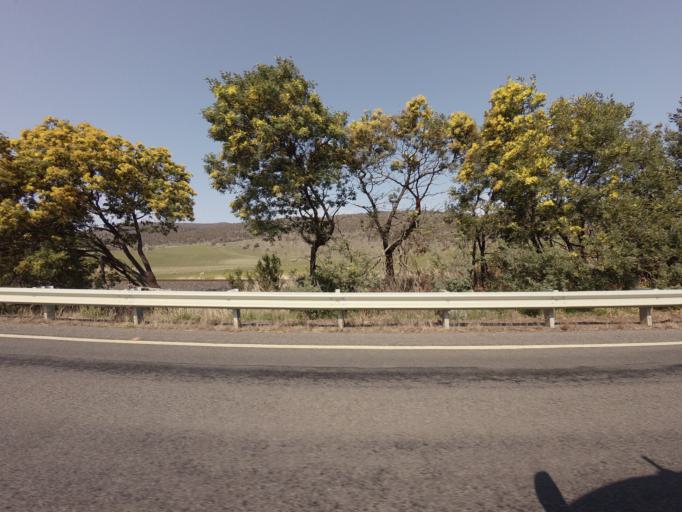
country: AU
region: Tasmania
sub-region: Northern Midlands
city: Evandale
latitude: -41.8121
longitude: 147.6148
